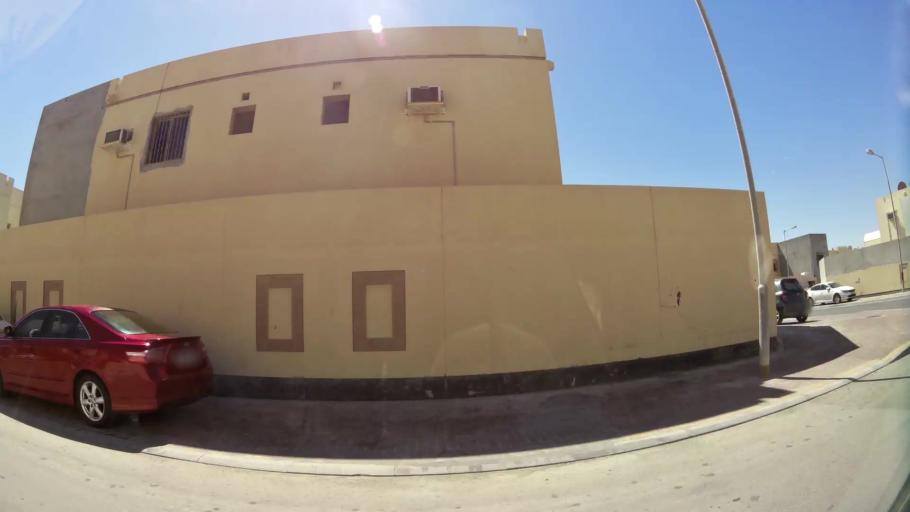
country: BH
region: Muharraq
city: Al Muharraq
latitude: 26.2681
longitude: 50.5977
